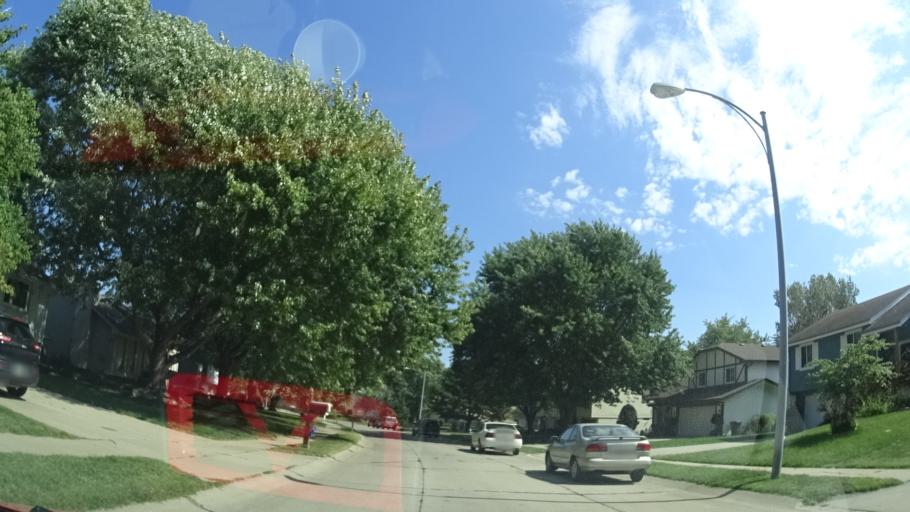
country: US
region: Nebraska
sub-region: Sarpy County
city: Offutt Air Force Base
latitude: 41.1323
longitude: -95.9539
